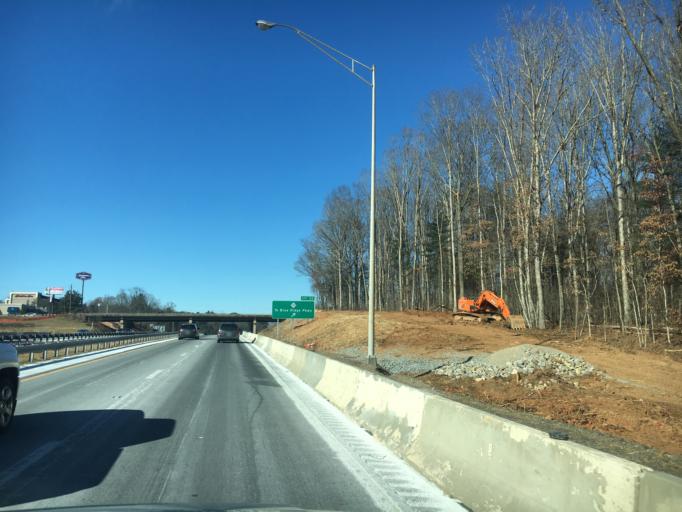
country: US
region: North Carolina
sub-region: Buncombe County
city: Bent Creek
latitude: 35.5322
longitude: -82.6012
